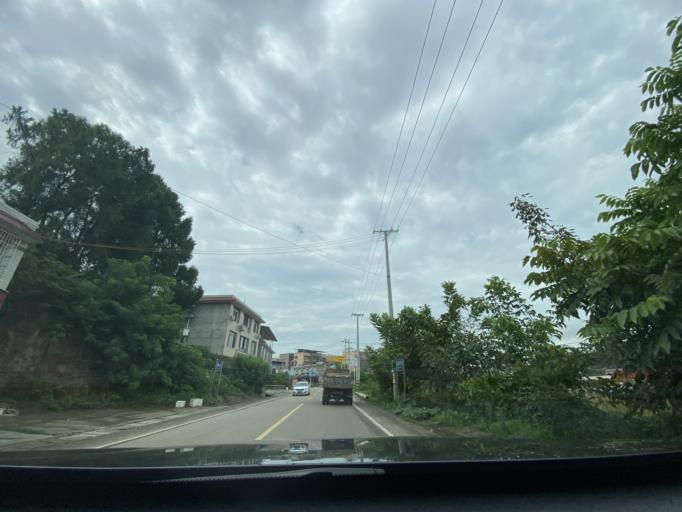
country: CN
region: Sichuan
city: Jiancheng
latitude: 30.4294
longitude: 104.6383
